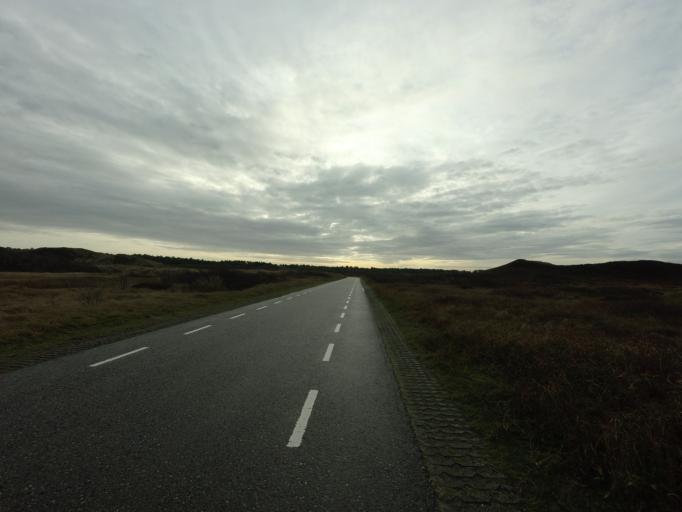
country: NL
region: North Holland
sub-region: Gemeente Texel
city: Den Burg
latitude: 53.0579
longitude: 4.7293
